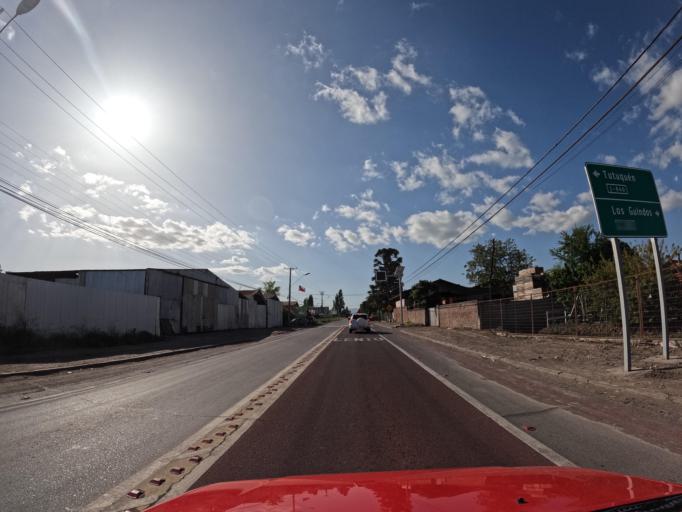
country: CL
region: Maule
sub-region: Provincia de Curico
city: Curico
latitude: -34.9474
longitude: -71.2589
